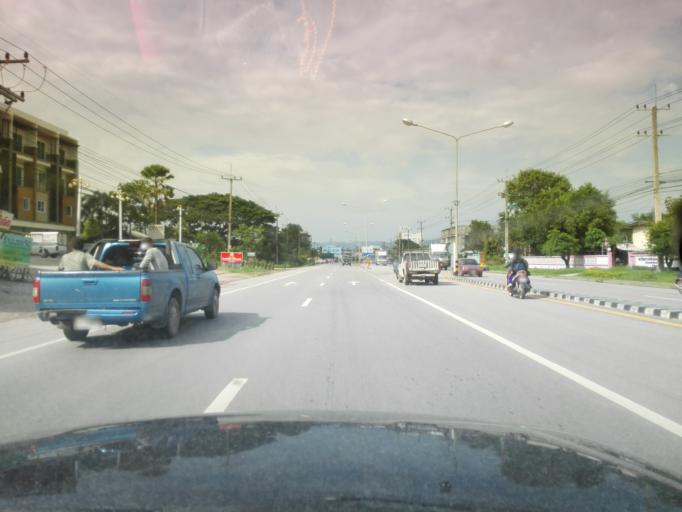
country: TH
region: Tak
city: Mae Sot
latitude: 16.7187
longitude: 98.5611
